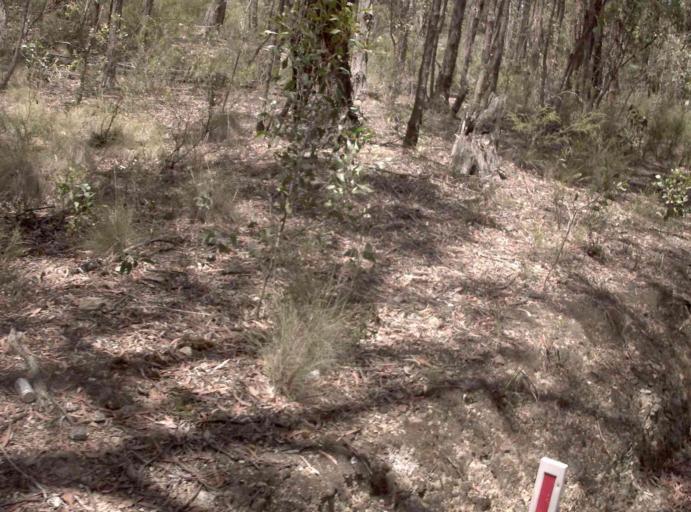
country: AU
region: Victoria
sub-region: East Gippsland
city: Lakes Entrance
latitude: -37.5883
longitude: 147.8920
